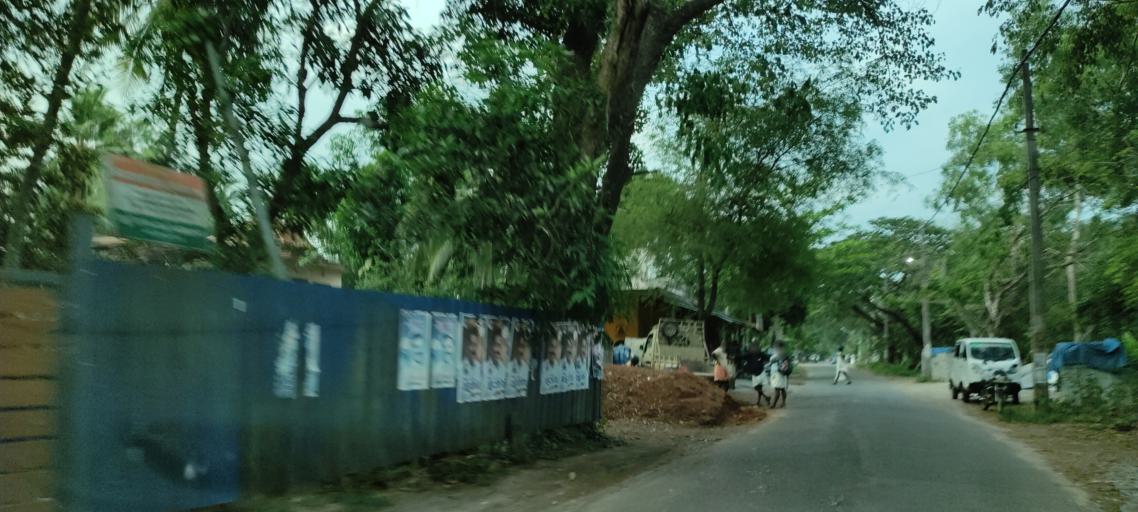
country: IN
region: Kerala
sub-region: Alappuzha
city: Shertallai
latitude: 9.6988
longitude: 76.3558
